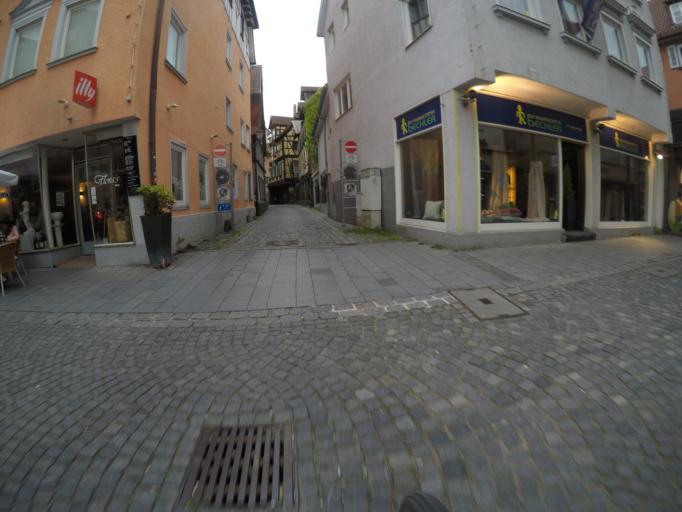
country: DE
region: Baden-Wuerttemberg
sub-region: Regierungsbezirk Stuttgart
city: Esslingen
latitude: 48.7395
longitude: 9.3059
